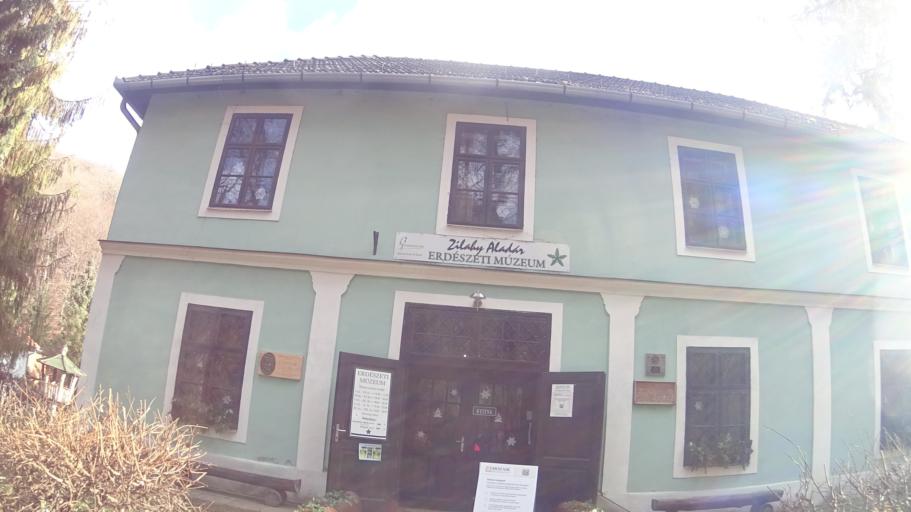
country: HU
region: Heves
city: Szilvasvarad
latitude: 48.0852
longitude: 20.4062
